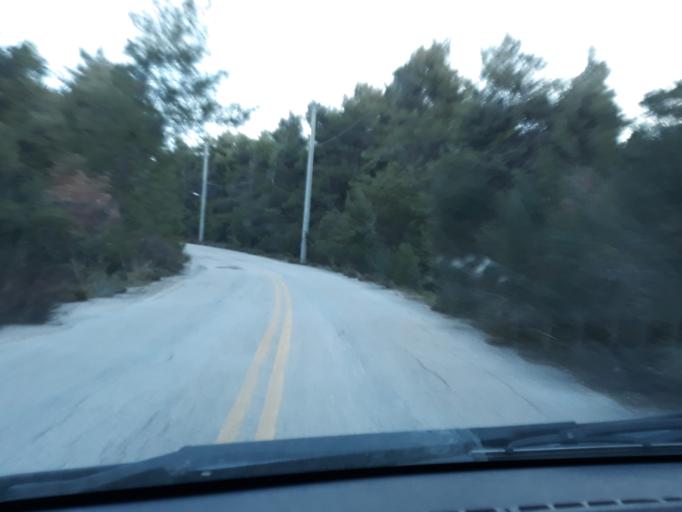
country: GR
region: Attica
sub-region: Nomarchia Anatolikis Attikis
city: Afidnes
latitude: 38.1987
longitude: 23.7911
